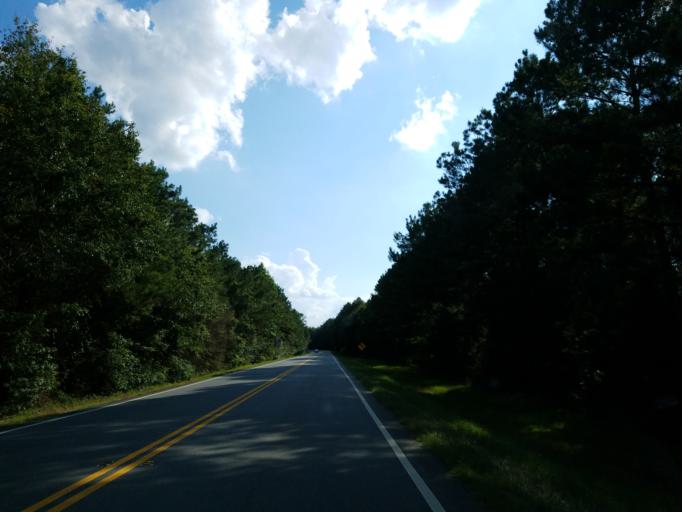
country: US
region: Georgia
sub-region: Crisp County
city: Cordele
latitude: 32.0055
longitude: -83.7398
